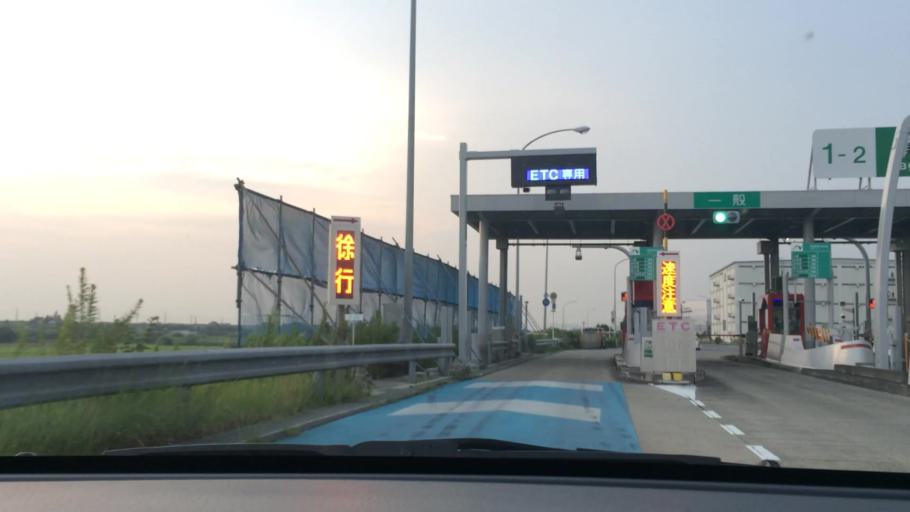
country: JP
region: Chiba
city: Nagareyama
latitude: 35.8794
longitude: 139.8989
